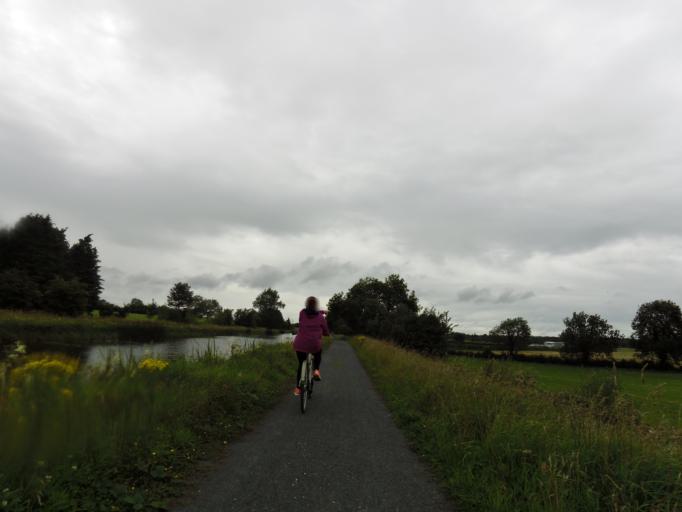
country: IE
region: Leinster
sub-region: An Iarmhi
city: Moate
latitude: 53.5887
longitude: -7.6384
